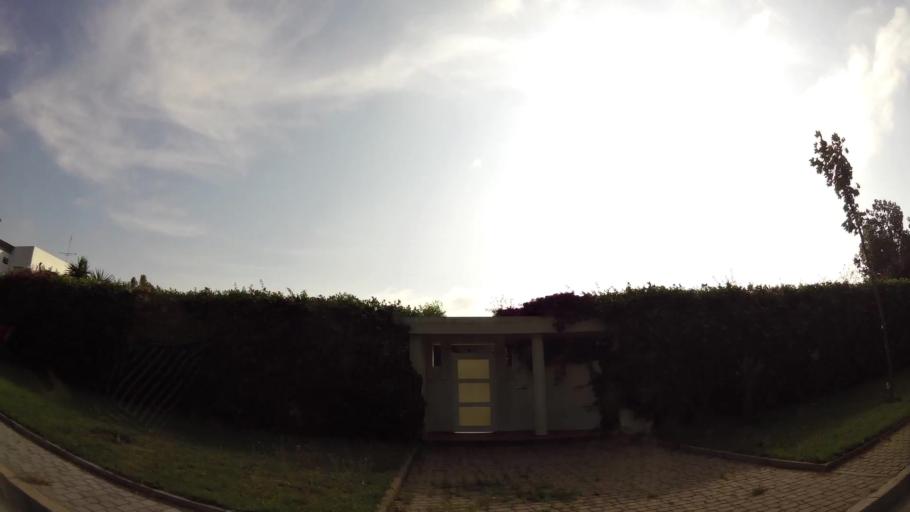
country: MA
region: Rabat-Sale-Zemmour-Zaer
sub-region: Rabat
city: Rabat
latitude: 33.9399
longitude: -6.8056
